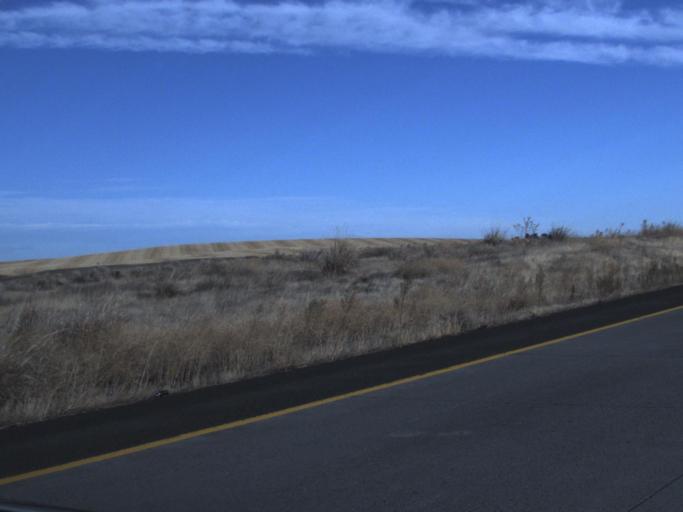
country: US
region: Washington
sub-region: Adams County
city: Ritzville
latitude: 46.9219
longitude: -118.5984
